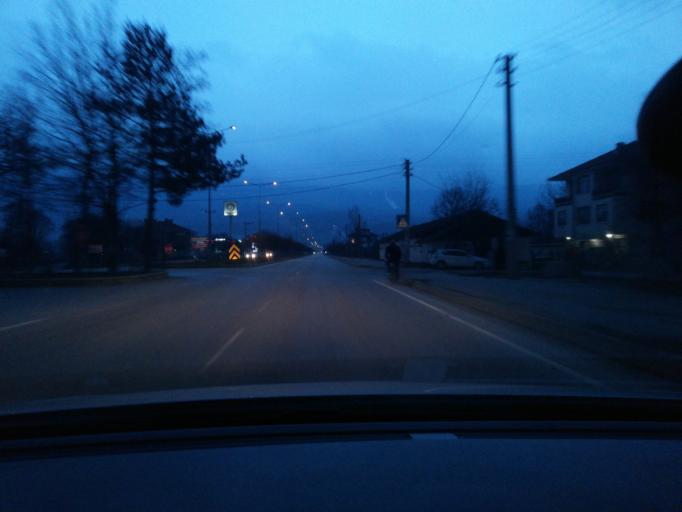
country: TR
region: Bolu
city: Bolu
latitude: 40.7046
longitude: 31.6176
